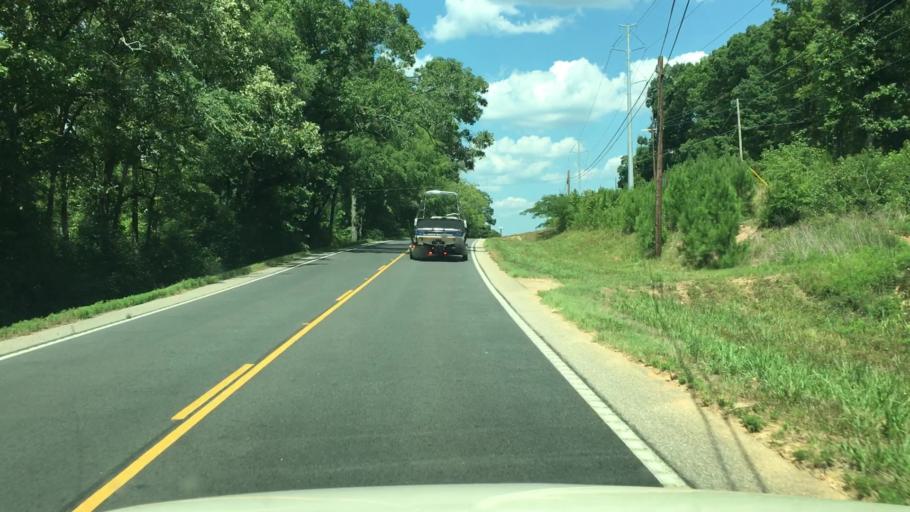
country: US
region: Arkansas
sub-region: Garland County
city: Lake Hamilton
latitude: 34.4004
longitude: -93.0987
